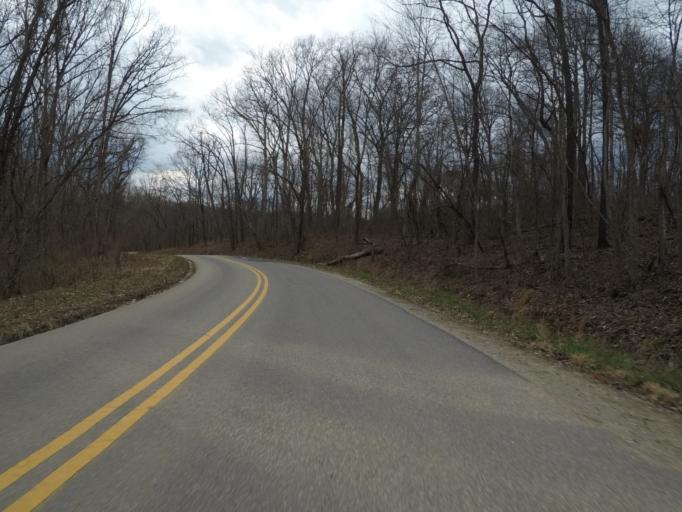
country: US
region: Ohio
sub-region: Lawrence County
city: Burlington
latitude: 38.4504
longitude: -82.5247
